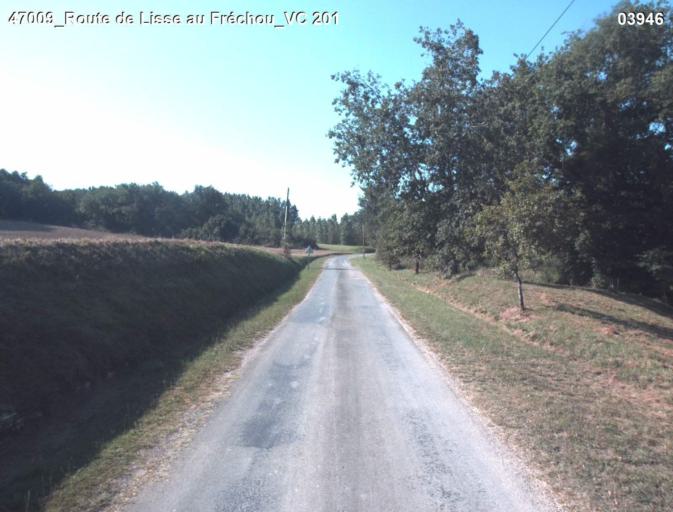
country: FR
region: Aquitaine
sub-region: Departement du Lot-et-Garonne
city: Mezin
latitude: 44.1040
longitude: 0.2760
